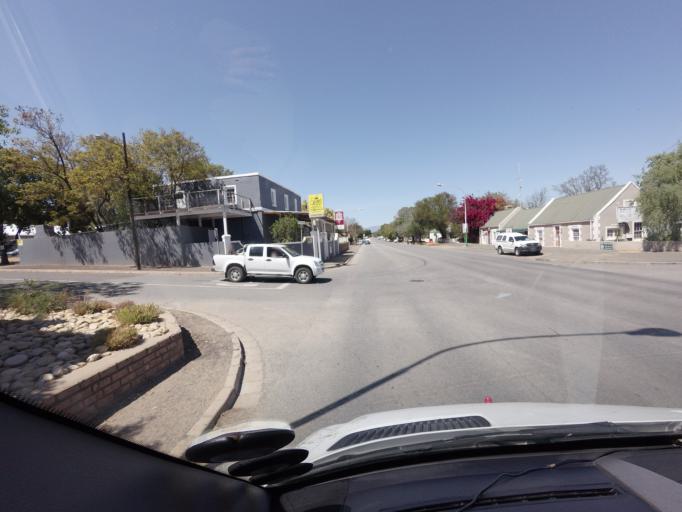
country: ZA
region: Western Cape
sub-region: Eden District Municipality
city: Oudtshoorn
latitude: -33.5798
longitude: 22.2052
